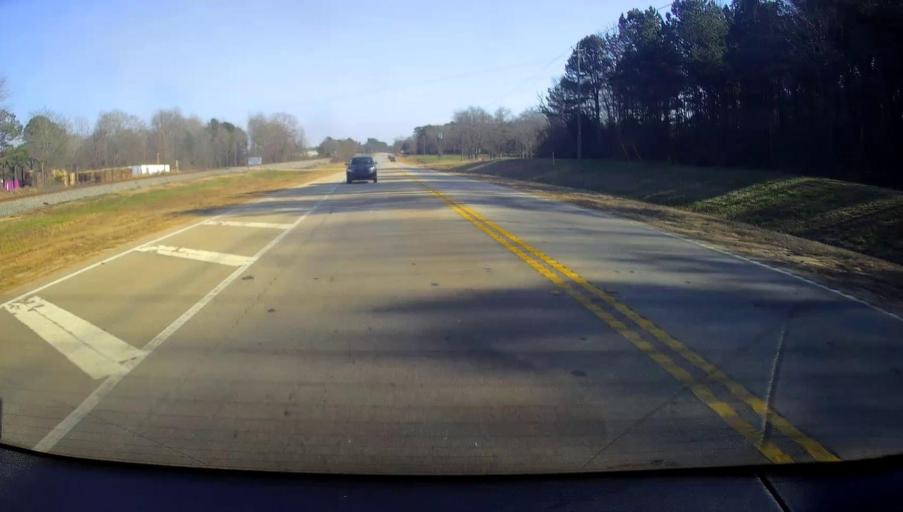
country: US
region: Georgia
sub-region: Butts County
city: Jackson
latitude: 33.3226
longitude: -83.9960
